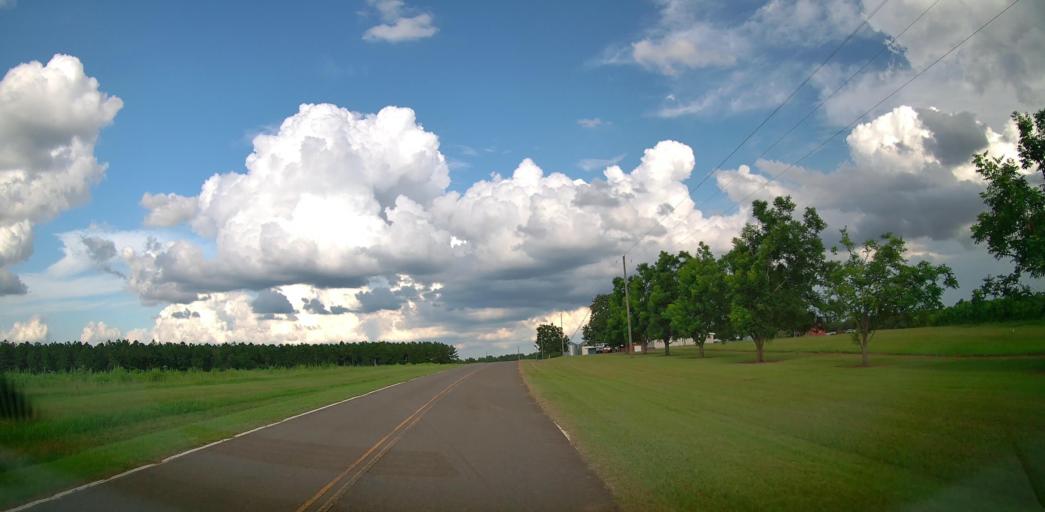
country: US
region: Georgia
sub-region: Bleckley County
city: Cochran
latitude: 32.4135
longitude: -83.4493
